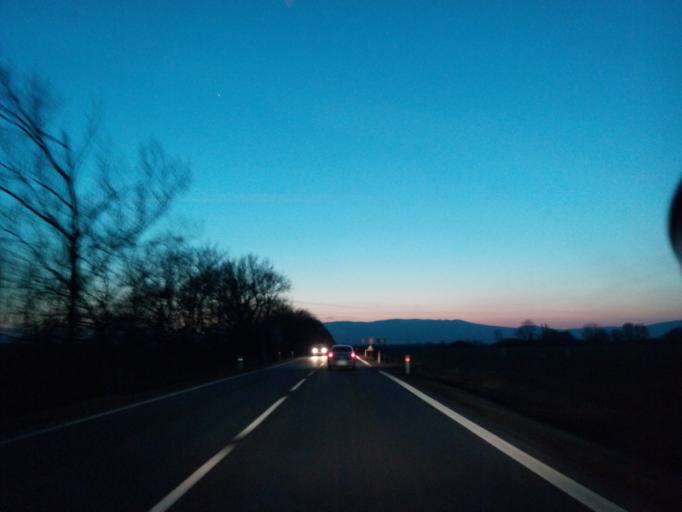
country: SK
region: Kosicky
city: Trebisov
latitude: 48.7005
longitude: 21.7412
